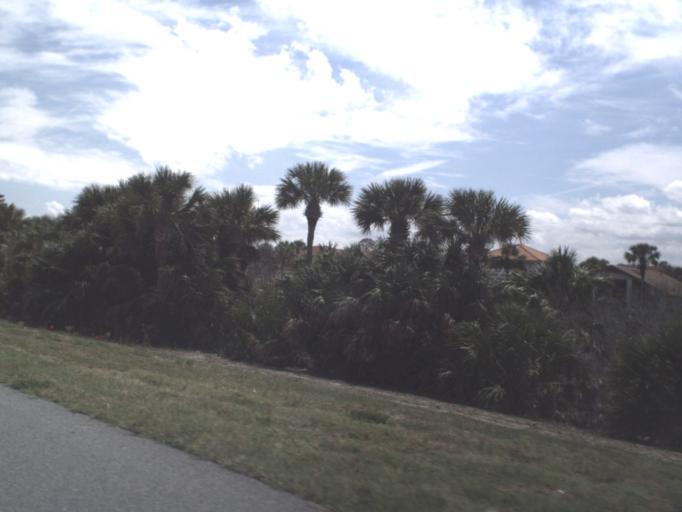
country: US
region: Florida
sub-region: Flagler County
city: Palm Coast
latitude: 29.6482
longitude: -81.2071
